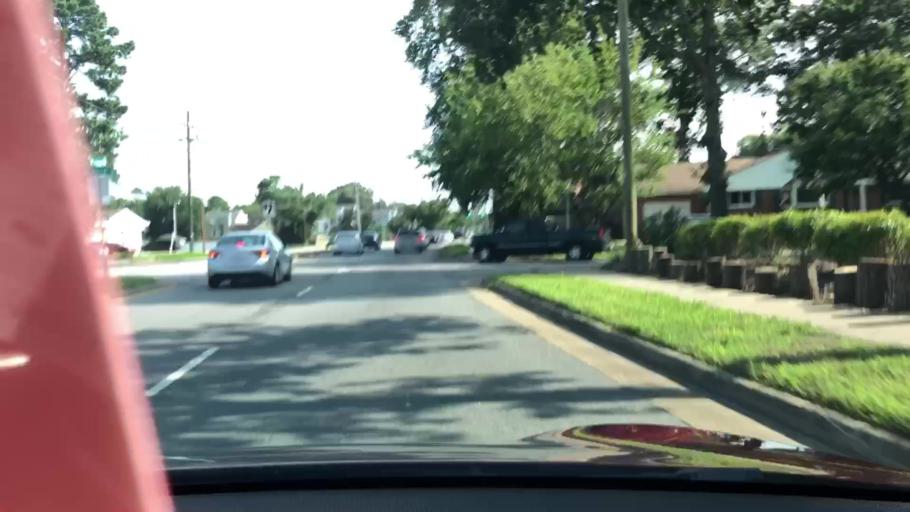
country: US
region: Virginia
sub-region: City of Virginia Beach
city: Virginia Beach
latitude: 36.8522
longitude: -75.9946
